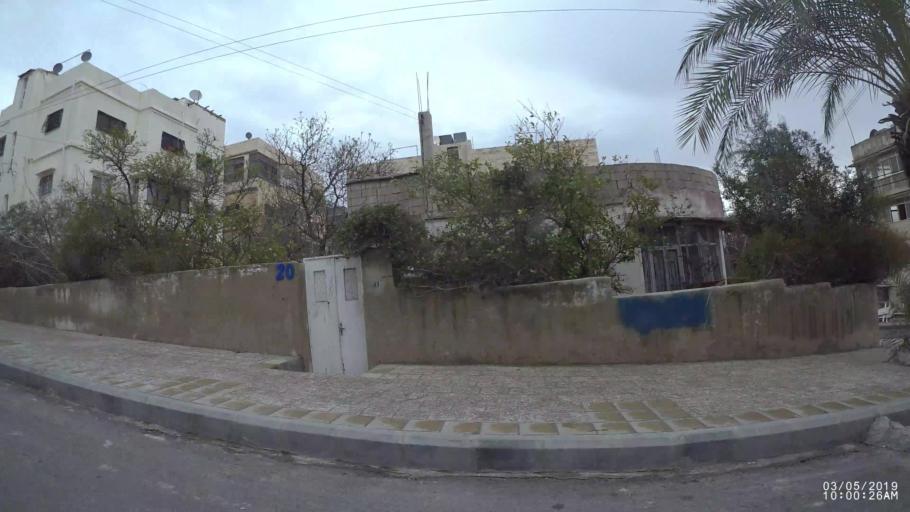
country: JO
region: Amman
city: Amman
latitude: 31.9803
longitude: 35.9273
